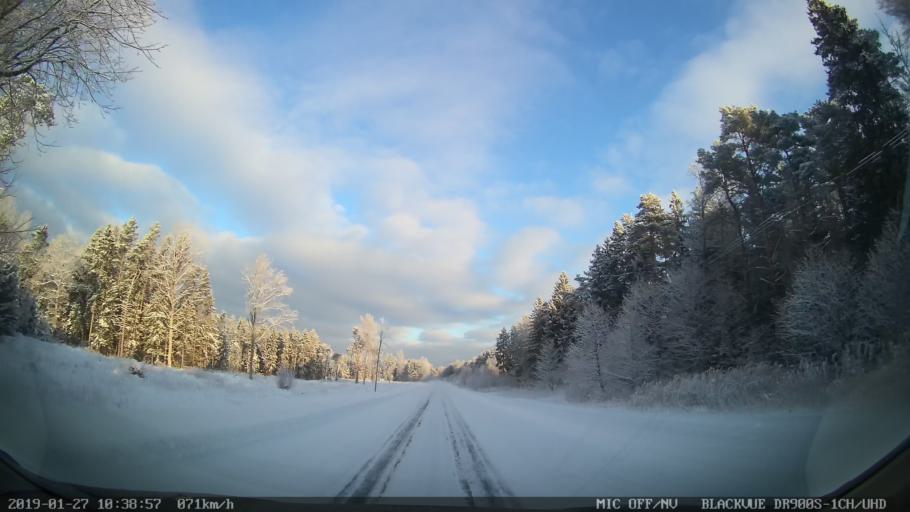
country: EE
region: Harju
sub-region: Raasiku vald
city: Raasiku
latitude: 59.4865
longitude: 25.2607
